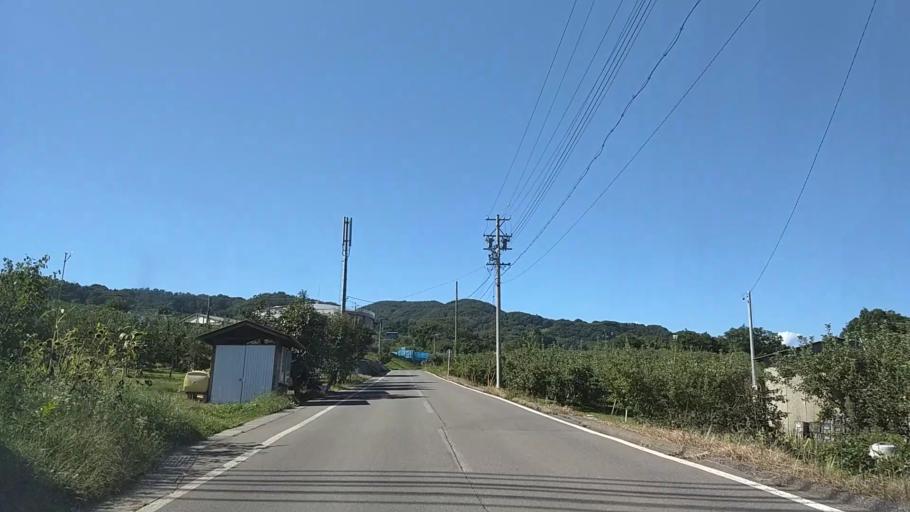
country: JP
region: Nagano
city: Nagano-shi
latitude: 36.5804
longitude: 138.1261
